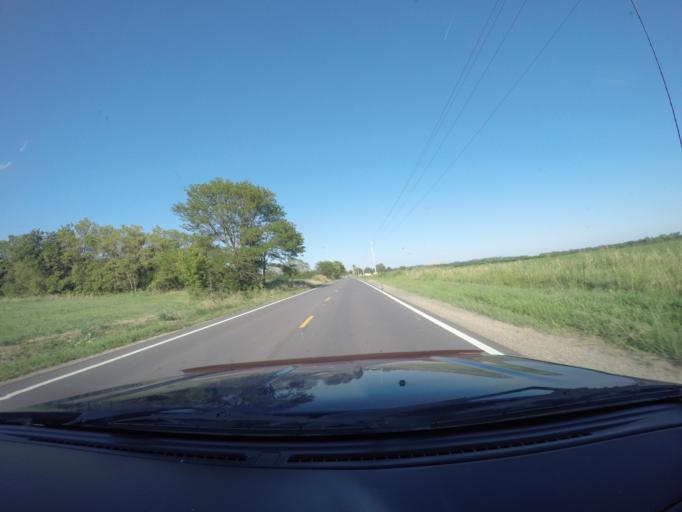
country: US
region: Kansas
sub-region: Douglas County
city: Lawrence
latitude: 39.0655
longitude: -95.3154
